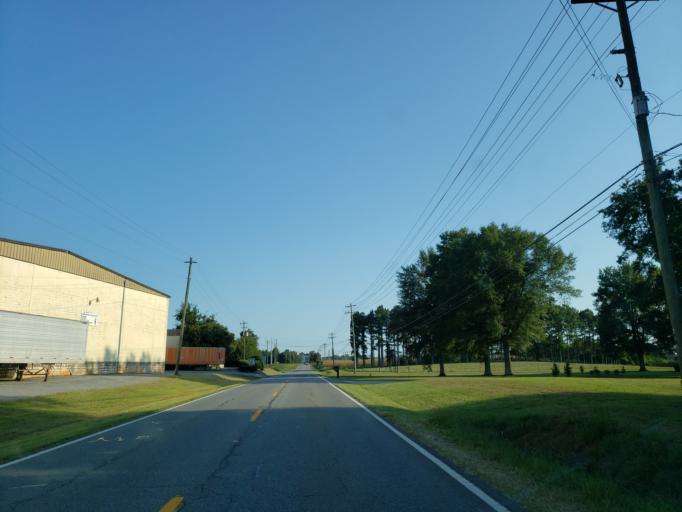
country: US
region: Georgia
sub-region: Murray County
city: Chatsworth
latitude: 34.7697
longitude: -84.8234
